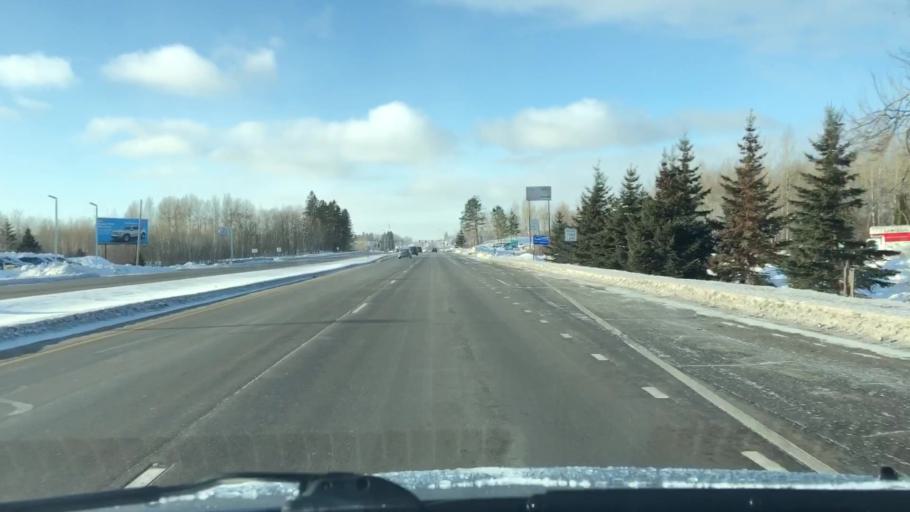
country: US
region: Minnesota
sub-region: Saint Louis County
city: Hermantown
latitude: 46.8164
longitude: -92.1772
